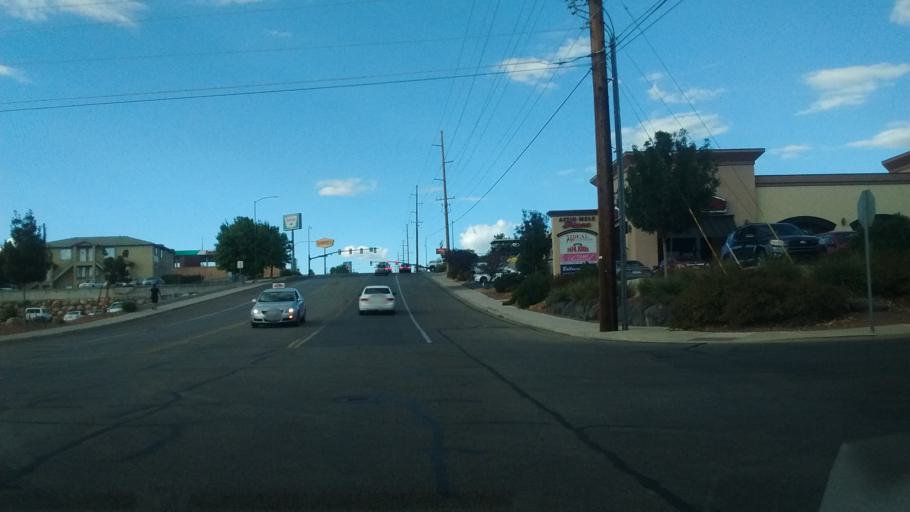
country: US
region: Utah
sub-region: Washington County
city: Saint George
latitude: 37.1081
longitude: -113.5621
